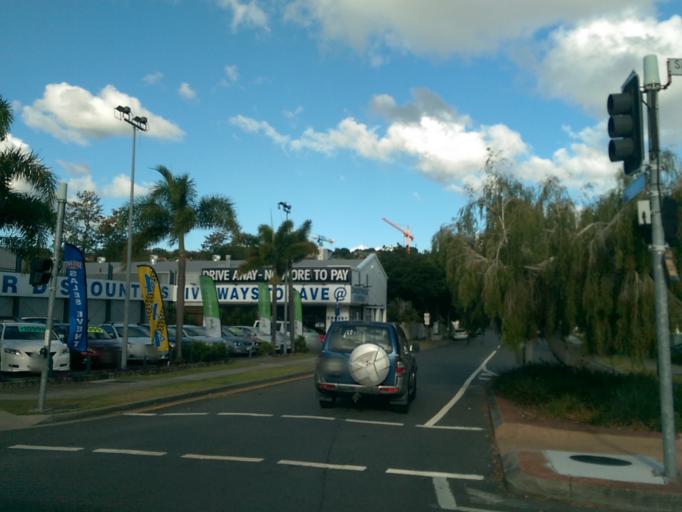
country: AU
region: Queensland
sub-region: Brisbane
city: Wooloowin
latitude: -27.4321
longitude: 153.0429
